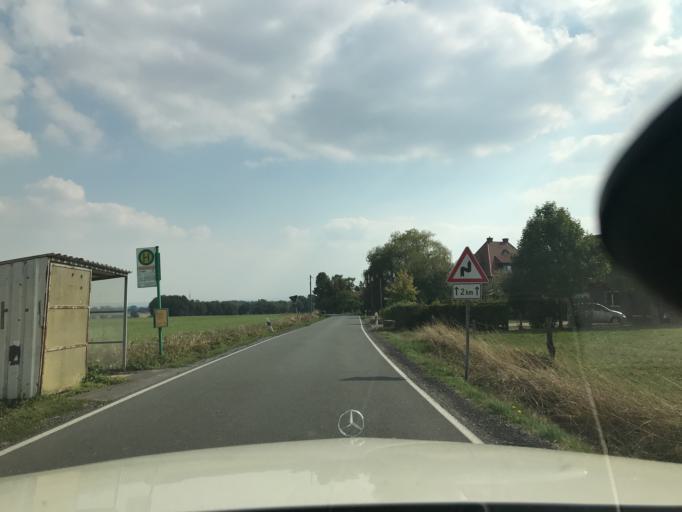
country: DE
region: North Rhine-Westphalia
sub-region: Regierungsbezirk Arnsberg
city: Werl
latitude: 51.6134
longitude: 7.8734
